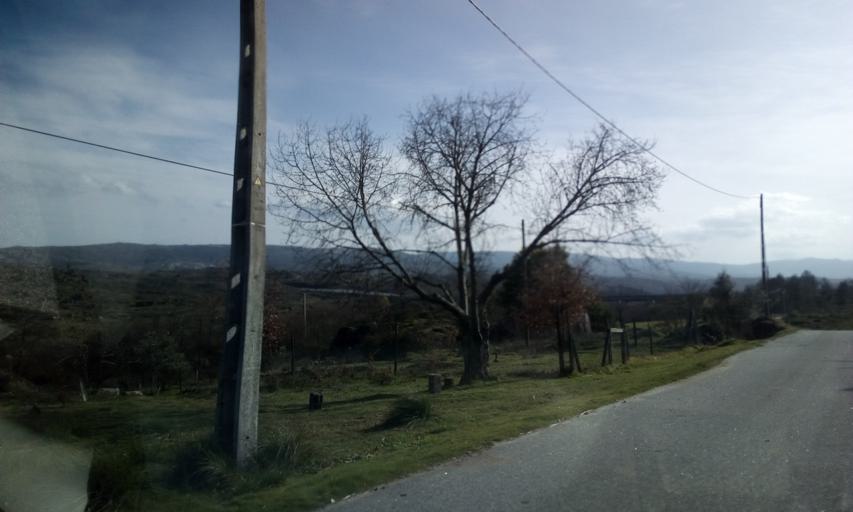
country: PT
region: Guarda
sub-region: Celorico da Beira
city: Celorico da Beira
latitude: 40.6369
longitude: -7.4327
